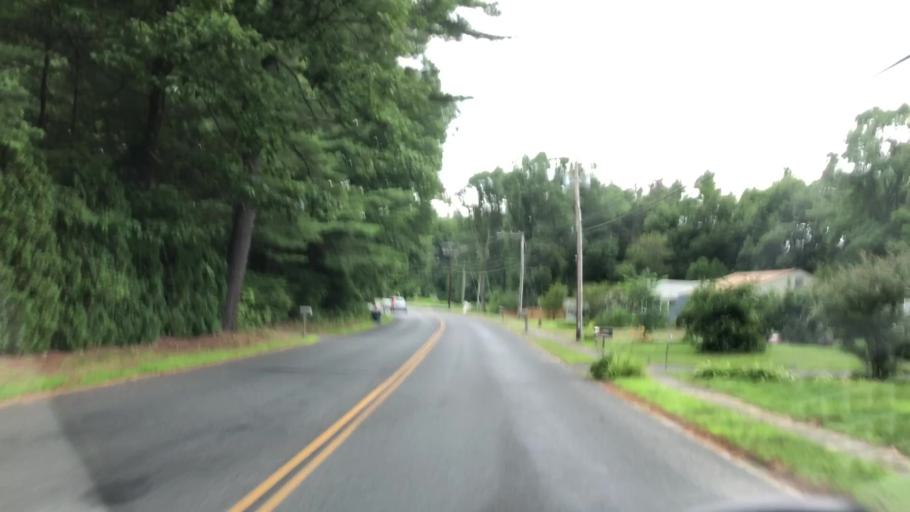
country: US
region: Massachusetts
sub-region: Hampshire County
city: Easthampton
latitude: 42.2343
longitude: -72.6860
